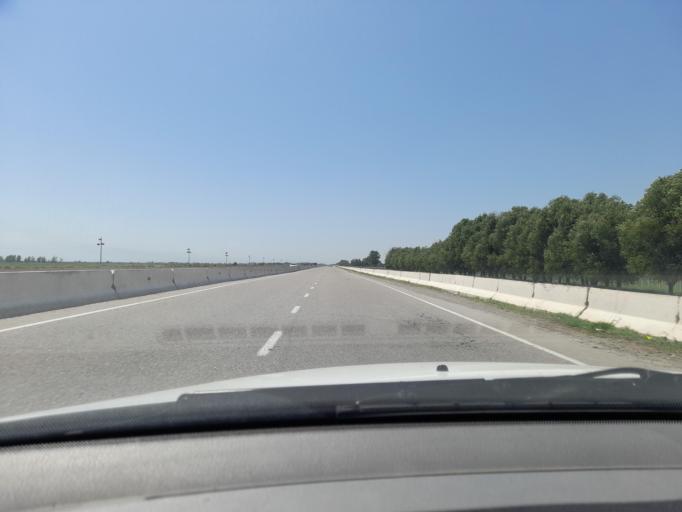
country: UZ
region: Jizzax
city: Paxtakor
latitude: 40.3511
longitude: 68.1314
